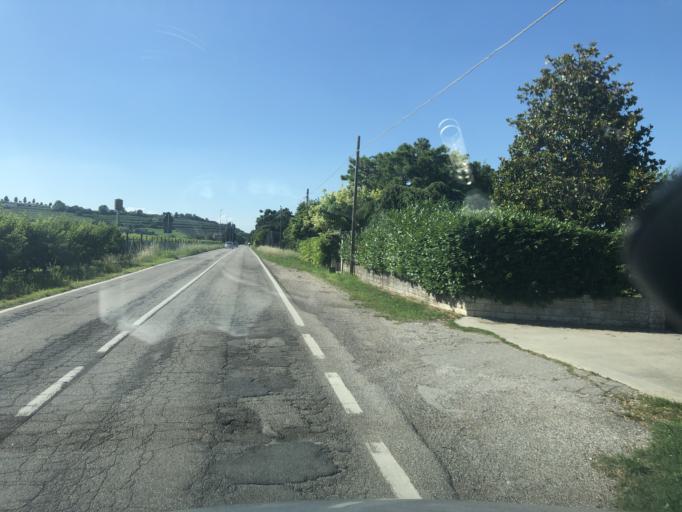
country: IT
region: Veneto
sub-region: Provincia di Verona
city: Villafranca di Verona
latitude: 45.3739
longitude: 10.8297
